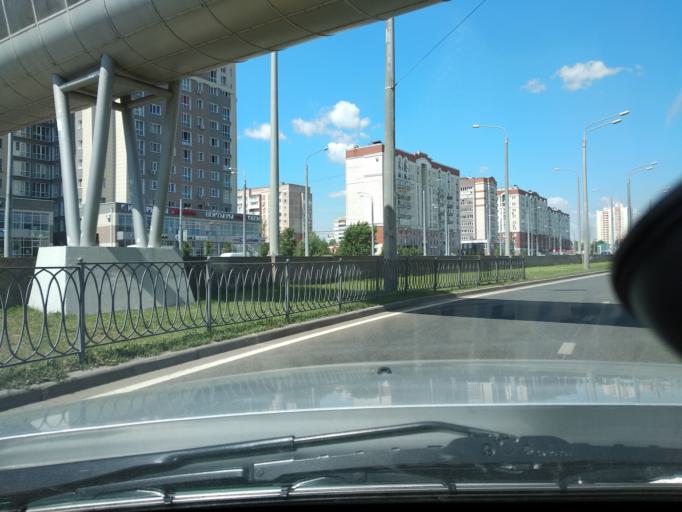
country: RU
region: Tatarstan
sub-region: Gorod Kazan'
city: Kazan
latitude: 55.8197
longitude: 49.1341
